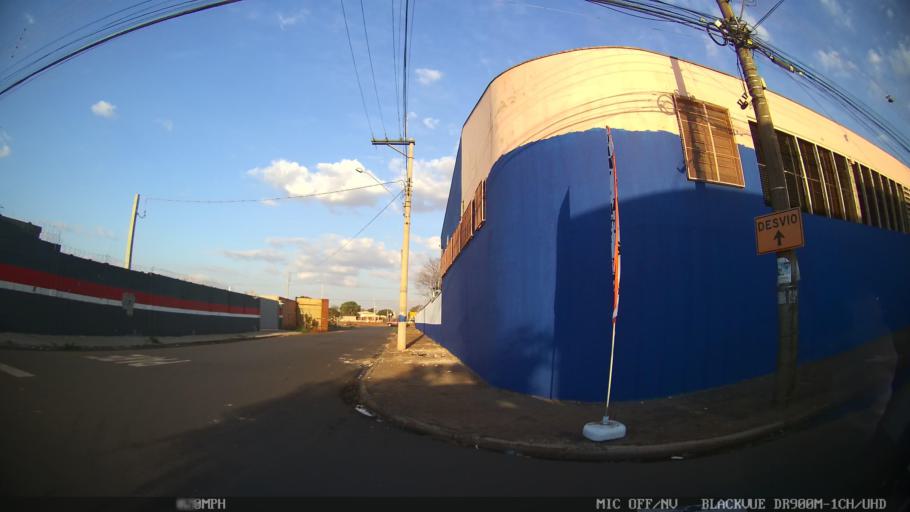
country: BR
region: Sao Paulo
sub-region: Ribeirao Preto
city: Ribeirao Preto
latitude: -21.1408
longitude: -47.7891
